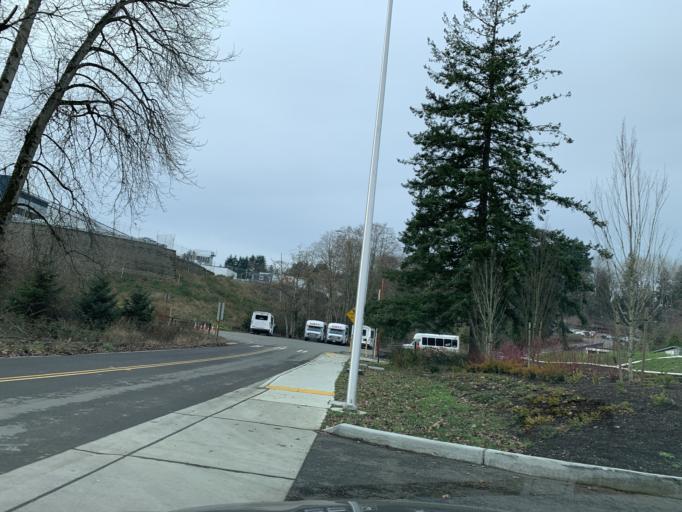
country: US
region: Washington
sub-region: King County
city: Boulevard Park
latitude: 47.4743
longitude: -122.3176
